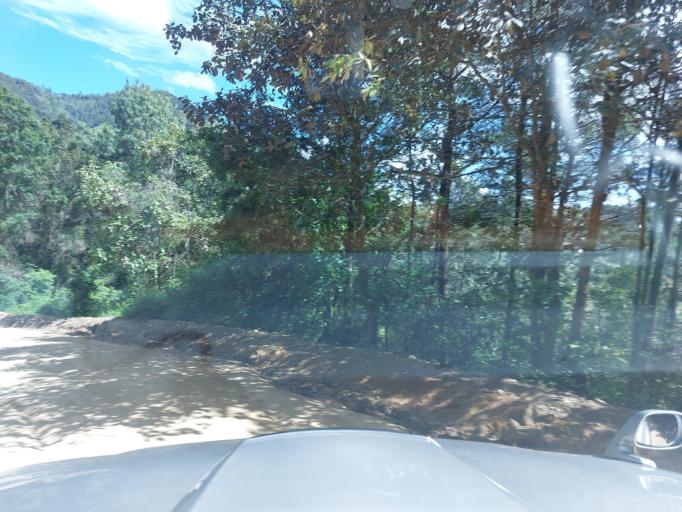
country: GT
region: Chimaltenango
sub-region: Municipio de San Juan Comalapa
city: Comalapa
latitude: 14.7588
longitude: -90.8869
